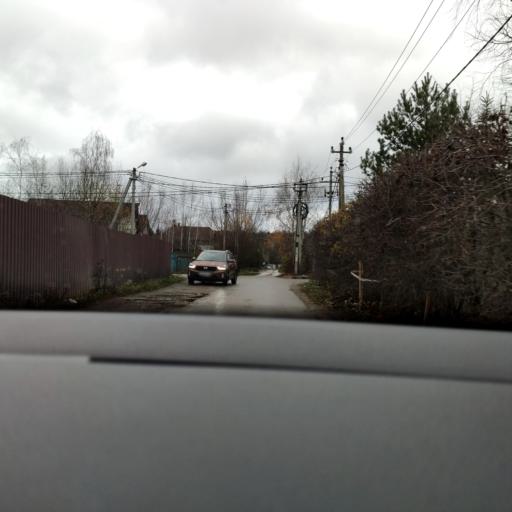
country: RU
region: Moscow
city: Gol'yanovo
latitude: 55.8333
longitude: 37.8349
